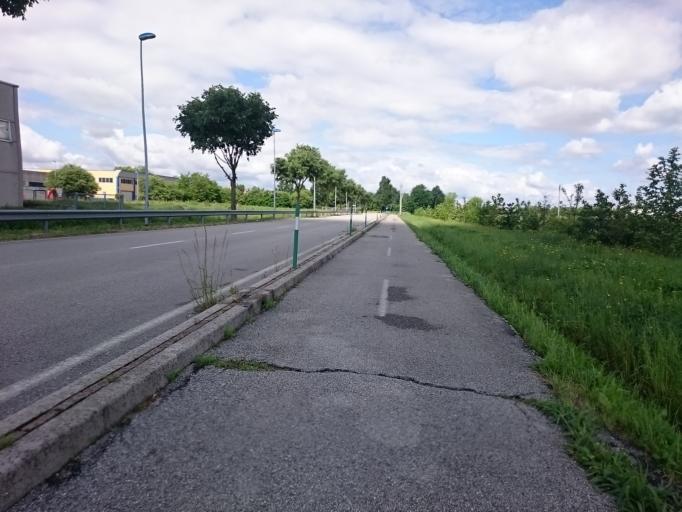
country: IT
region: Veneto
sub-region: Provincia di Padova
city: Mestrino
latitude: 45.4412
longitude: 11.7714
